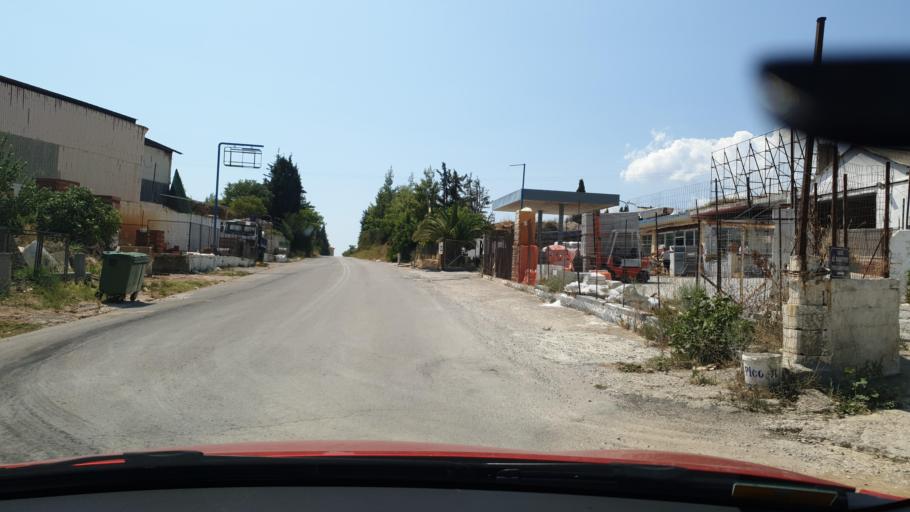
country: GR
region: Central Greece
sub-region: Nomos Evvoias
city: Kymi
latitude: 38.6236
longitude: 24.0980
